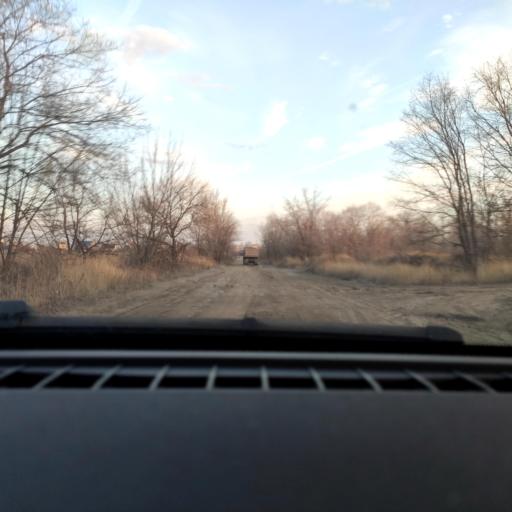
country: RU
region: Voronezj
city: Maslovka
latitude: 51.6107
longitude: 39.2669
